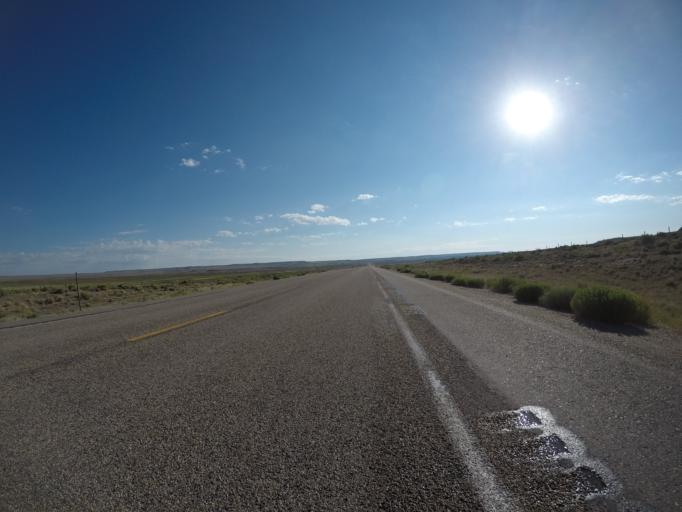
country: US
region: Wyoming
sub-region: Lincoln County
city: Kemmerer
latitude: 41.9802
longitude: -110.1940
